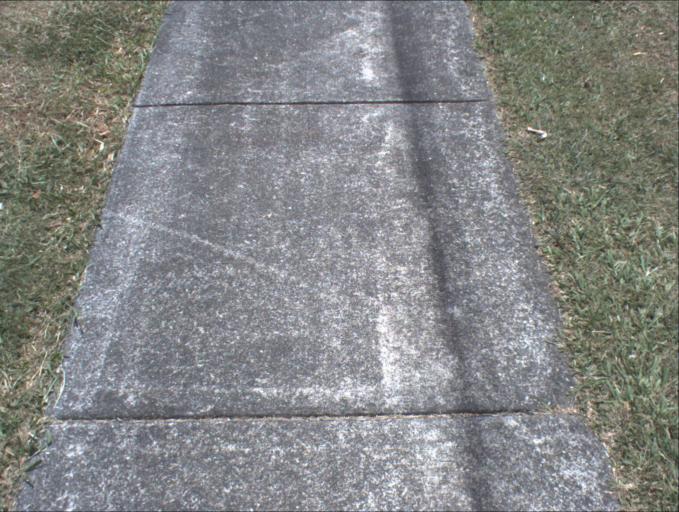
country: AU
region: Queensland
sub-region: Logan
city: Rochedale South
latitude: -27.5986
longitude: 153.1094
